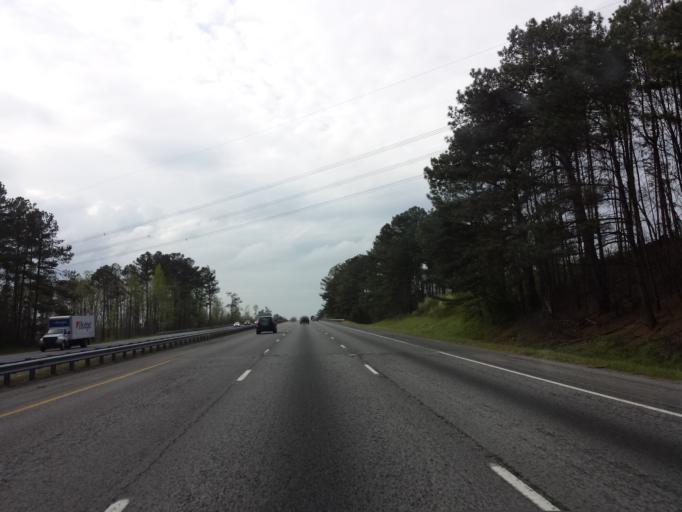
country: US
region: Georgia
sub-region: Monroe County
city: Forsyth
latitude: 33.1390
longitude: -84.0222
